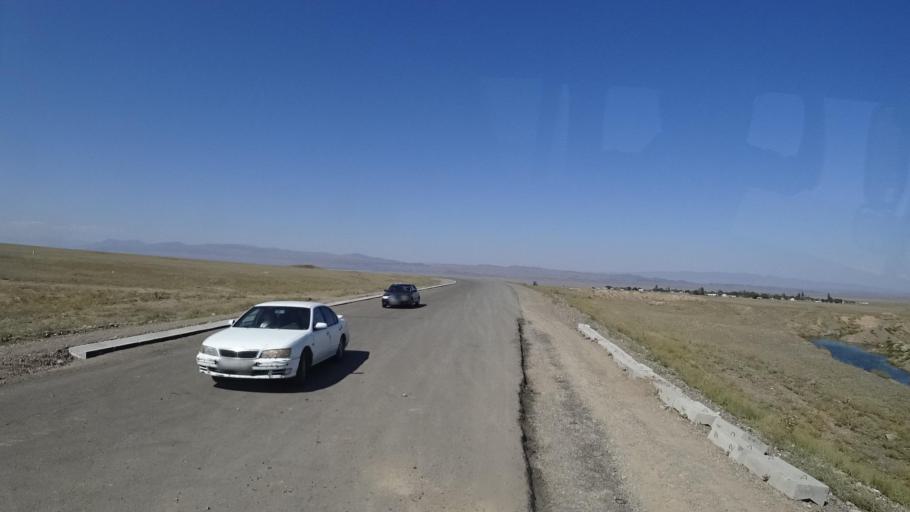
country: KZ
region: Almaty Oblysy
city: Kegen
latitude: 43.2006
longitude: 79.1222
